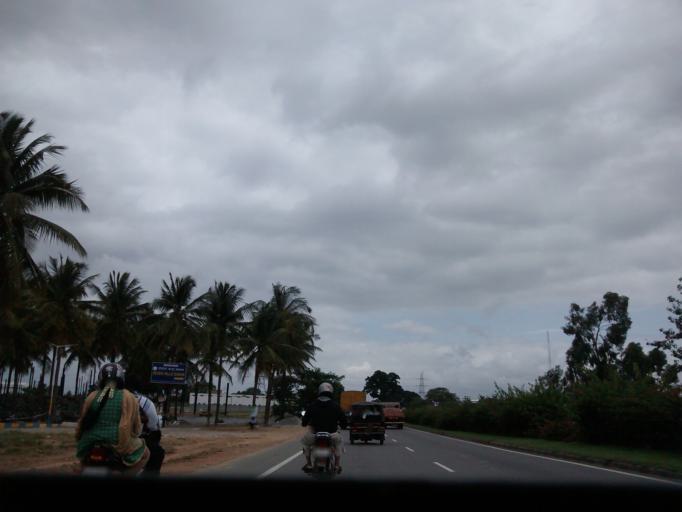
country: IN
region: Karnataka
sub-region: Bangalore Rural
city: Nelamangala
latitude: 13.1284
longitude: 77.3614
